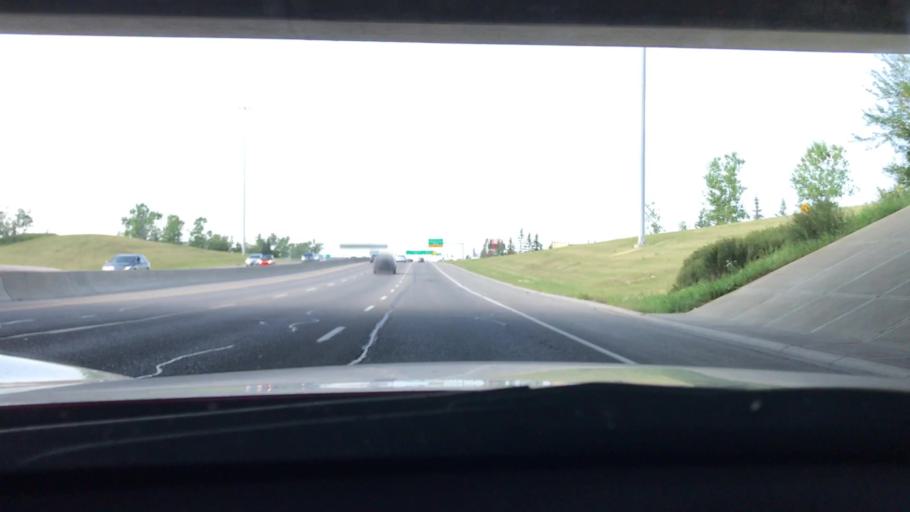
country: CA
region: Alberta
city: Calgary
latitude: 51.0088
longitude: -114.1179
